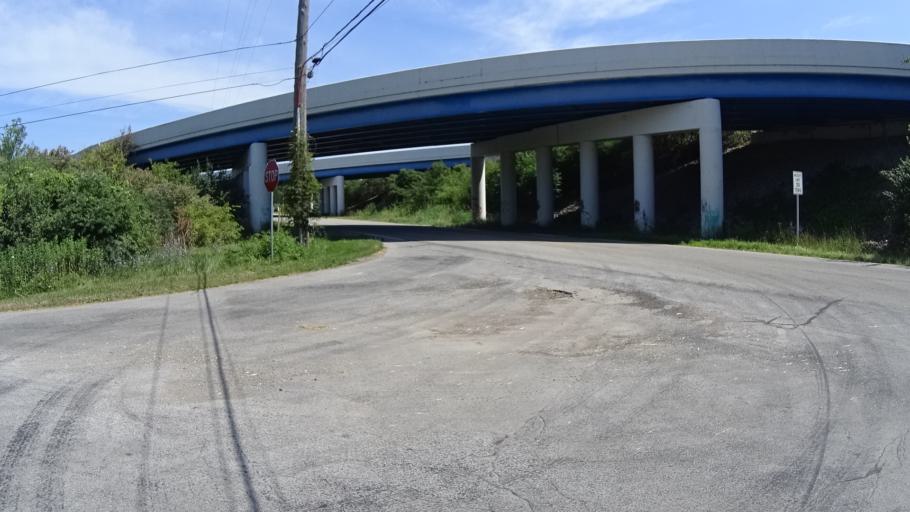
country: US
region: Ohio
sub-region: Erie County
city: Sandusky
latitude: 41.4297
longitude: -82.7724
